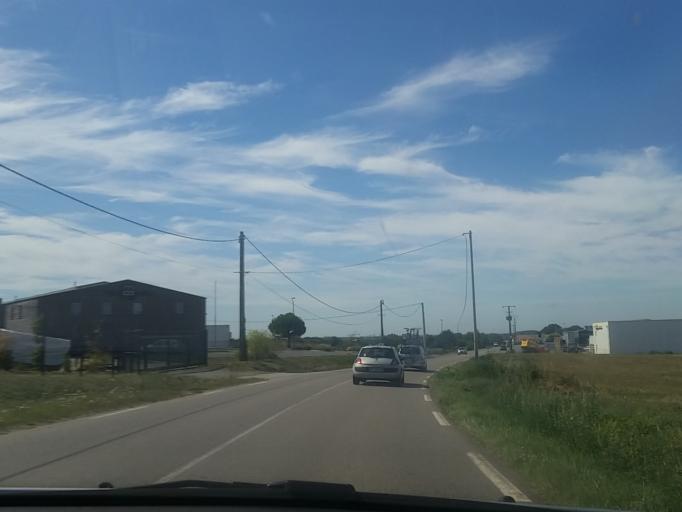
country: FR
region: Pays de la Loire
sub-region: Departement de la Loire-Atlantique
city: Saint-Pere-en-Retz
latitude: 47.1950
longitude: -2.0284
